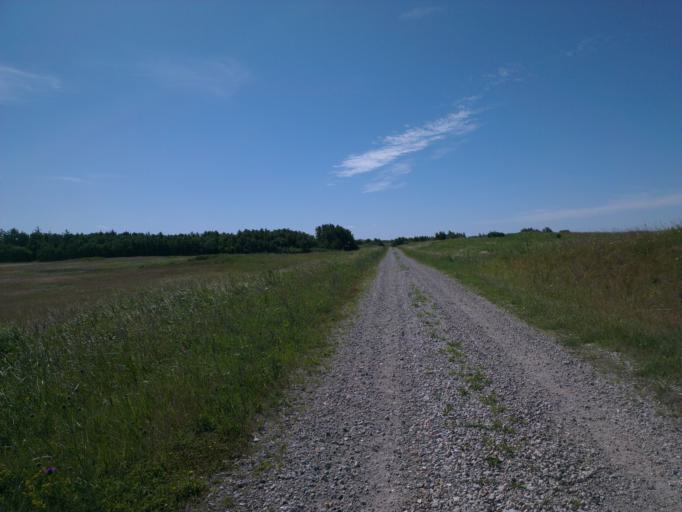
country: DK
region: Capital Region
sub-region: Frederikssund Kommune
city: Jaegerspris
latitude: 55.8872
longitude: 11.9332
